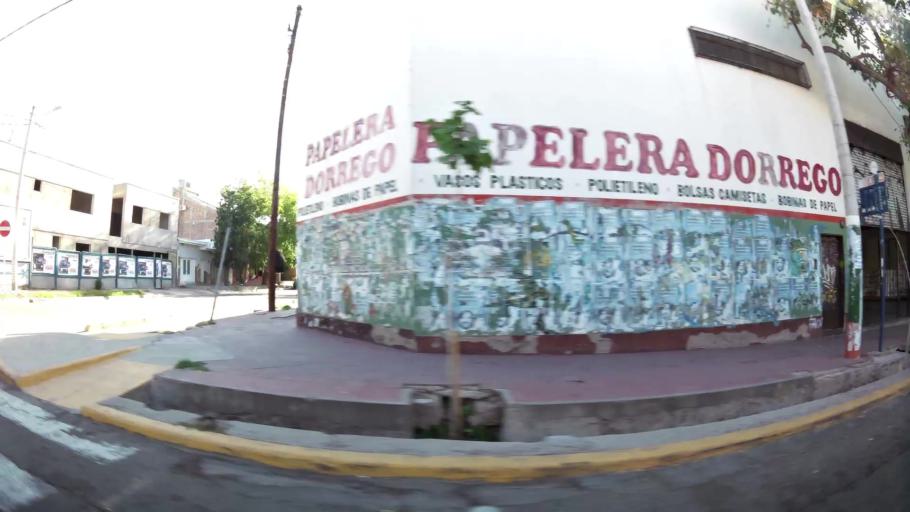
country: AR
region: Mendoza
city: Mendoza
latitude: -32.9018
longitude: -68.8288
